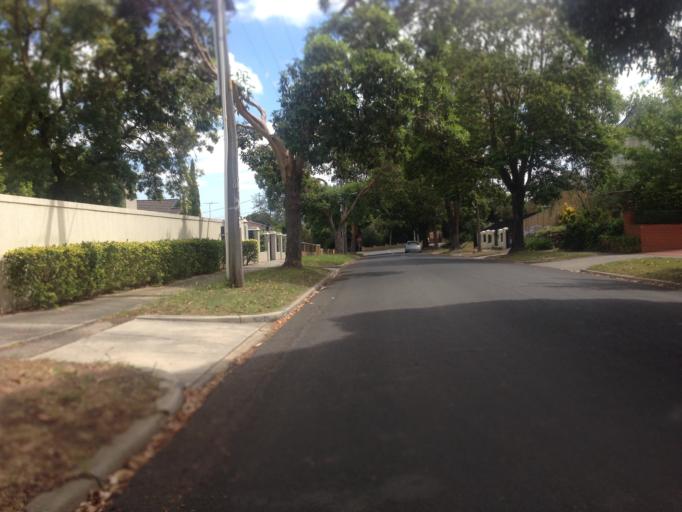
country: AU
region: Victoria
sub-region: Boroondara
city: Balwyn North
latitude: -37.7854
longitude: 145.0796
